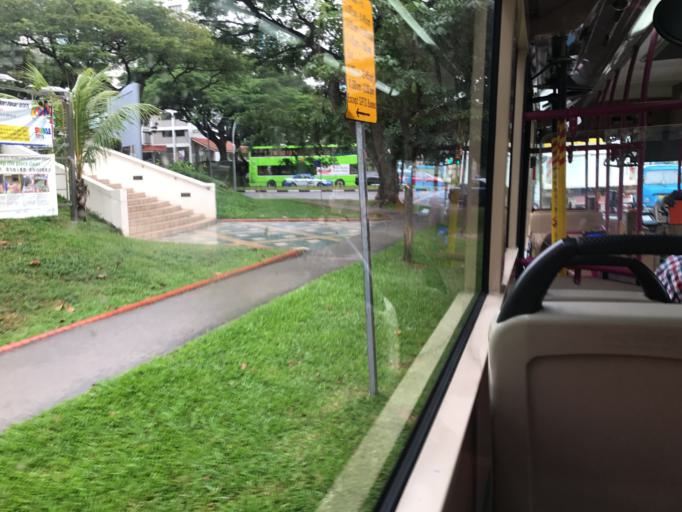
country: SG
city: Singapore
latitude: 1.3300
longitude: 103.9266
